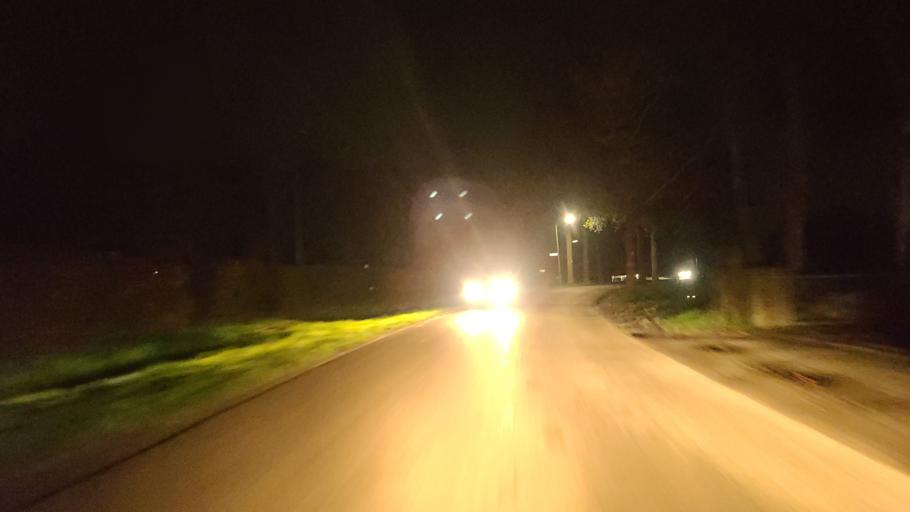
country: NL
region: Limburg
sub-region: Gemeente Gennep
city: Gennep
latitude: 51.7222
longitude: 5.9582
